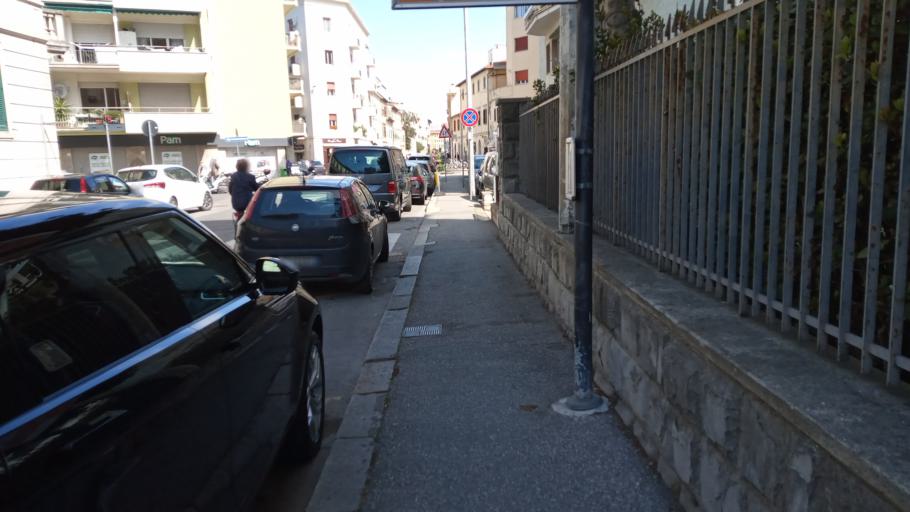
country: IT
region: Tuscany
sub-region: Provincia di Livorno
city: Livorno
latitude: 43.5401
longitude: 10.3128
